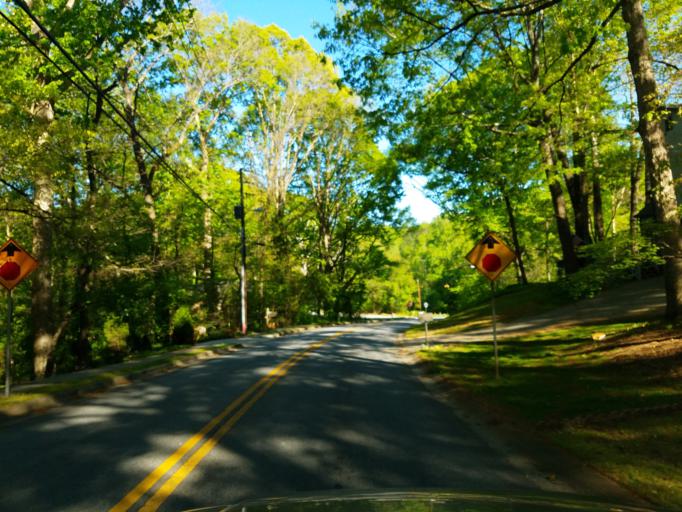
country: US
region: Georgia
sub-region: Cobb County
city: Smyrna
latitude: 33.8566
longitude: -84.5310
